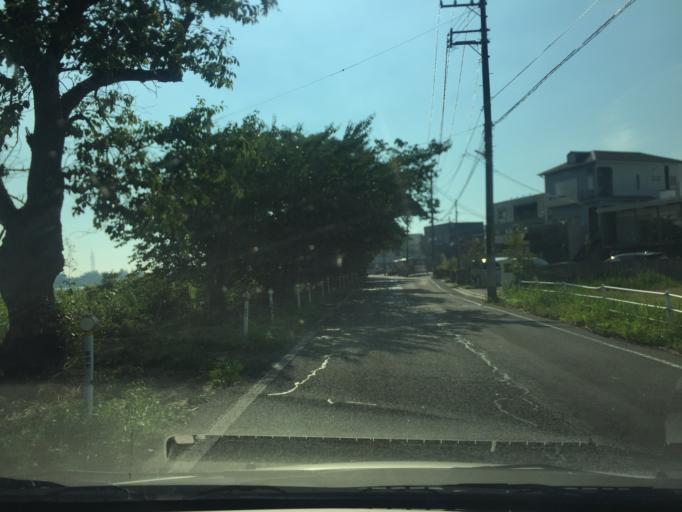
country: JP
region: Niigata
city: Niigata-shi
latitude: 37.8943
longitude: 139.0604
